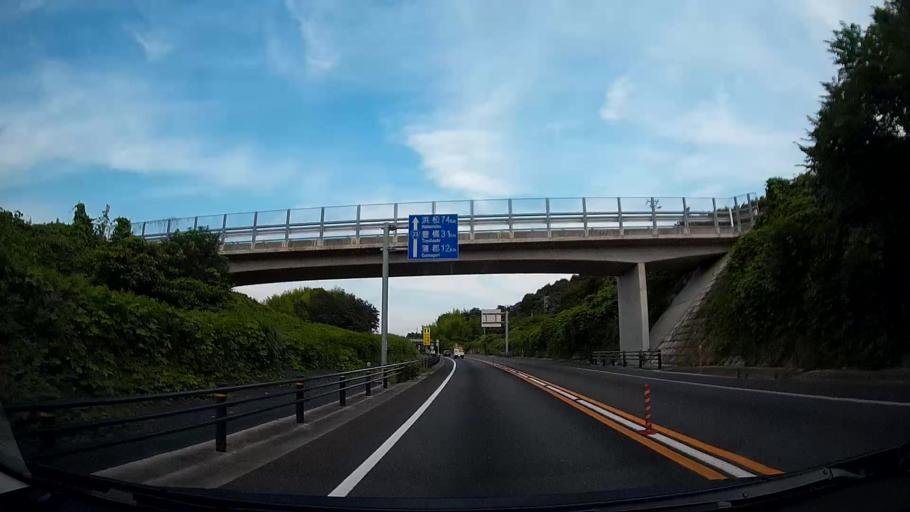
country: JP
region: Aichi
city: Nishio
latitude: 34.8518
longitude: 137.1306
